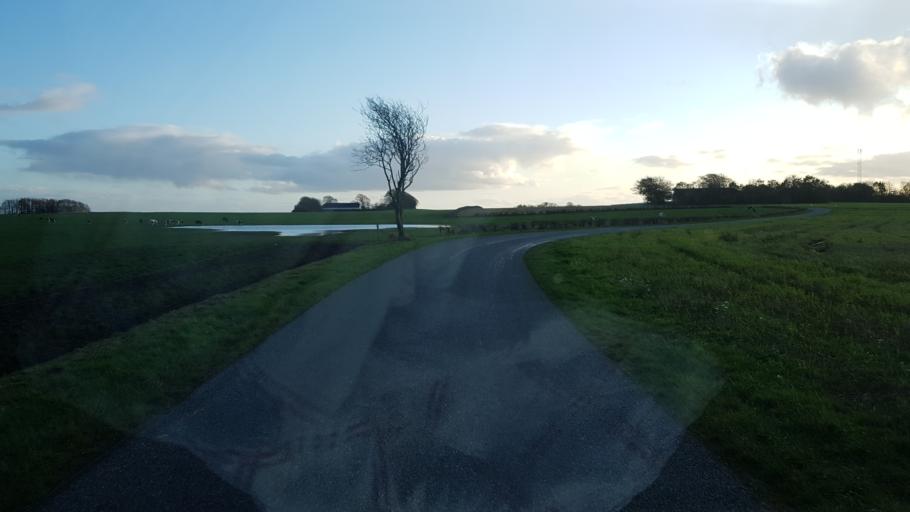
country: DK
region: South Denmark
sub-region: Vejen Kommune
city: Holsted
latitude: 55.4600
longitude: 8.9454
